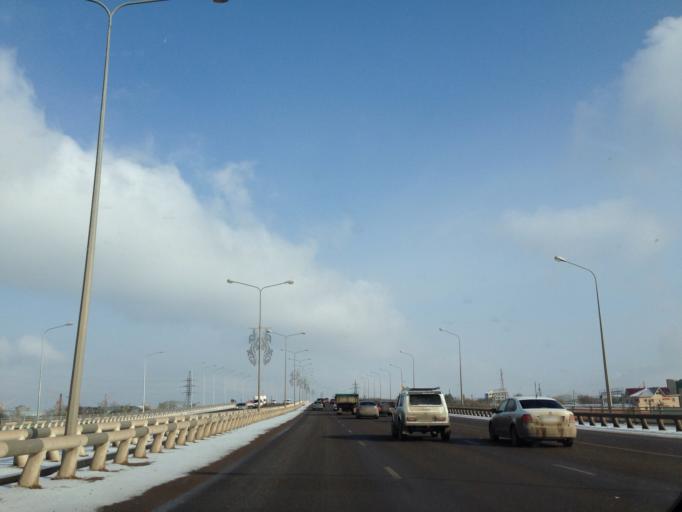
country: KZ
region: Astana Qalasy
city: Astana
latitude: 51.1823
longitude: 71.4447
